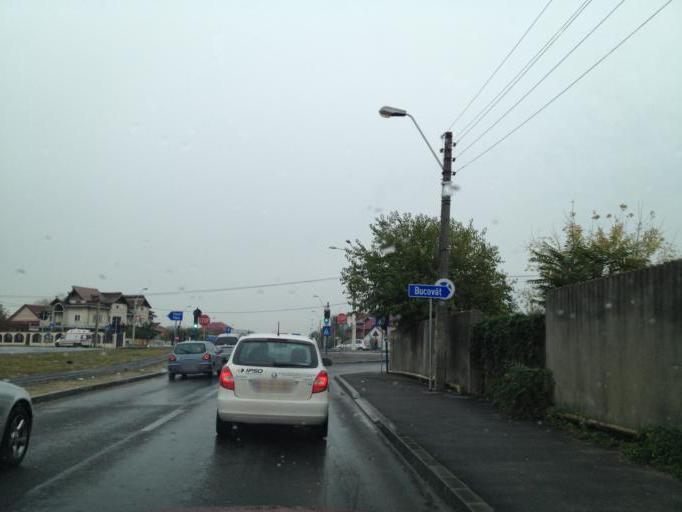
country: RO
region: Dolj
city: Craiova
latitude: 44.3120
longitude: 23.7805
